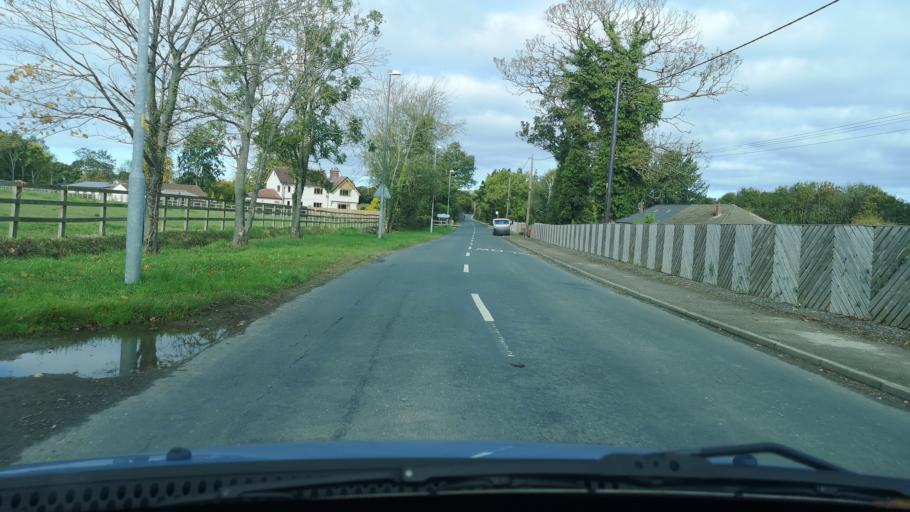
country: GB
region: England
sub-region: City and Borough of Wakefield
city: Featherstone
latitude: 53.6833
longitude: -1.3809
